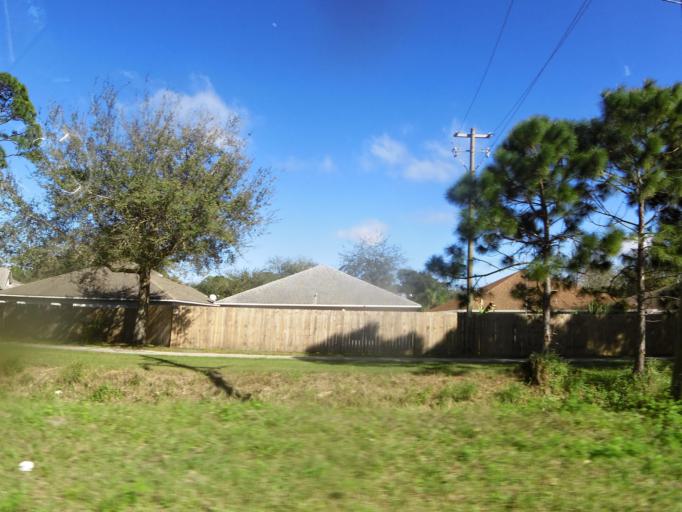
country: US
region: Florida
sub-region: Brevard County
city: Port Saint John
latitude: 28.5422
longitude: -80.8064
